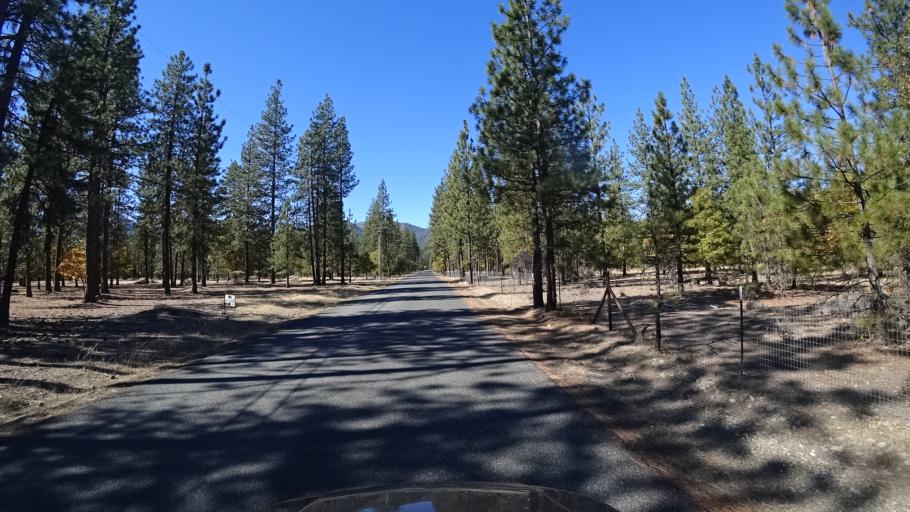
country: US
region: California
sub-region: Siskiyou County
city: Yreka
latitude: 41.5412
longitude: -122.9388
